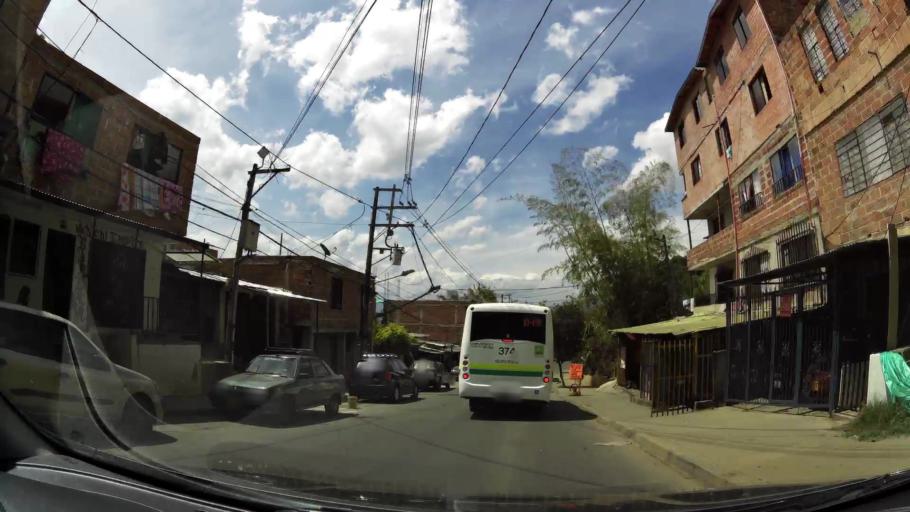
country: CO
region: Antioquia
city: Bello
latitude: 6.3483
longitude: -75.5519
